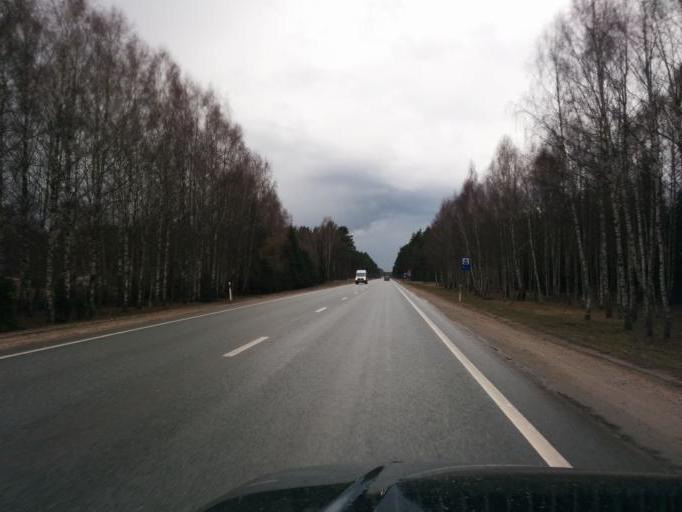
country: LV
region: Babite
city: Pinki
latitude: 56.8834
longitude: 23.9464
